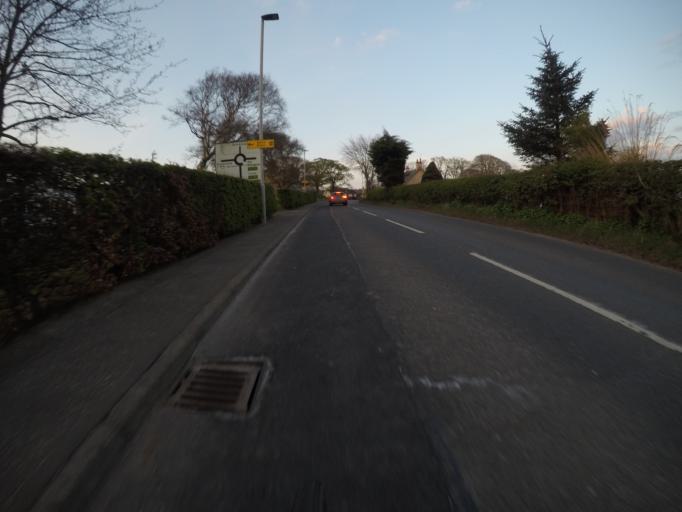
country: GB
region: Scotland
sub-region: South Ayrshire
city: Troon
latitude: 55.5490
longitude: -4.6242
